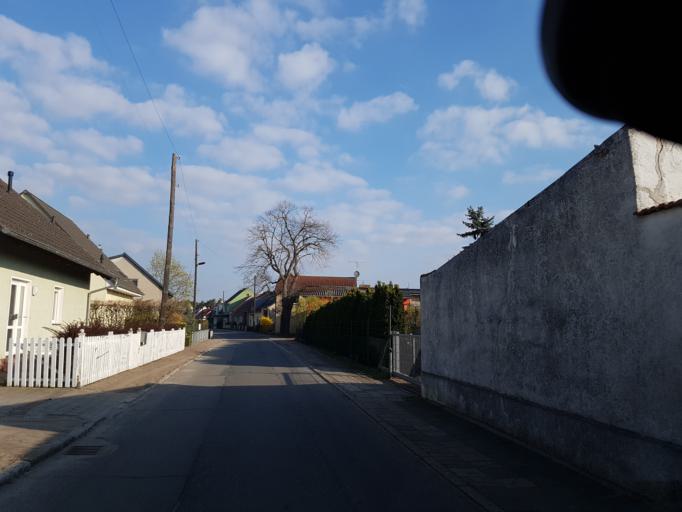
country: DE
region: Brandenburg
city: Bruck
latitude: 52.1781
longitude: 12.7525
